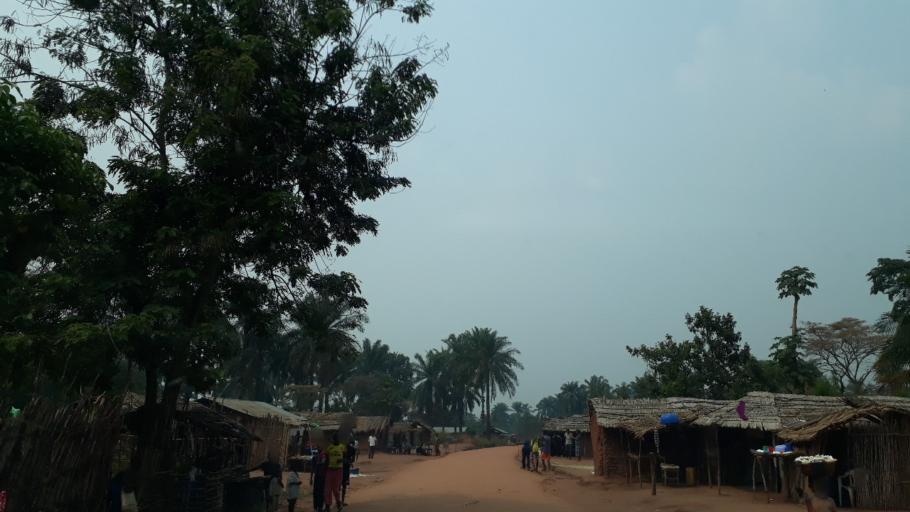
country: CD
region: Kasai-Occidental
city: Tshikapa
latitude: -6.4880
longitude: 20.4177
